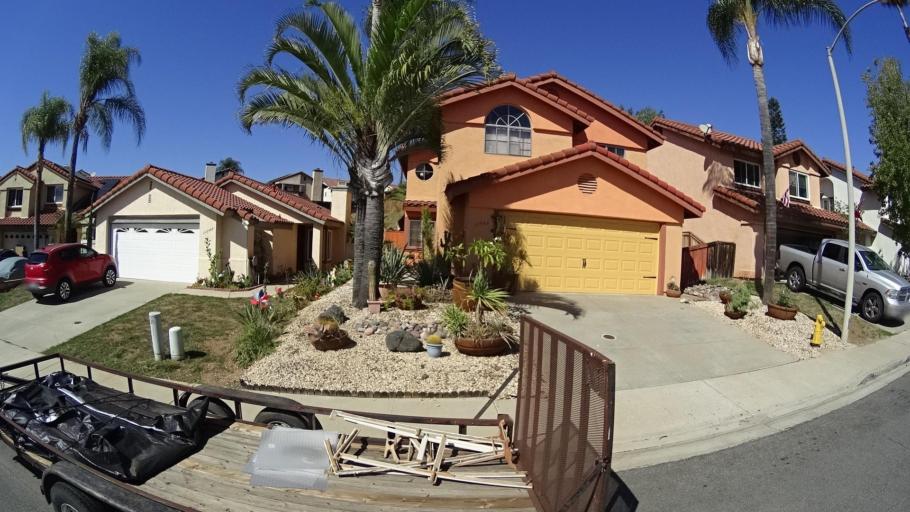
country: US
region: California
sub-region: San Diego County
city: Rancho San Diego
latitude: 32.7488
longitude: -116.9370
